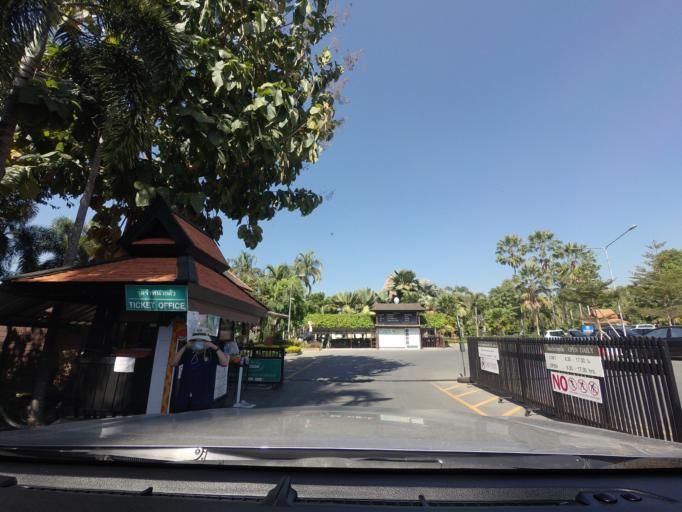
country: TH
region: Chiang Mai
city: San Sai
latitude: 18.8576
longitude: 99.0999
